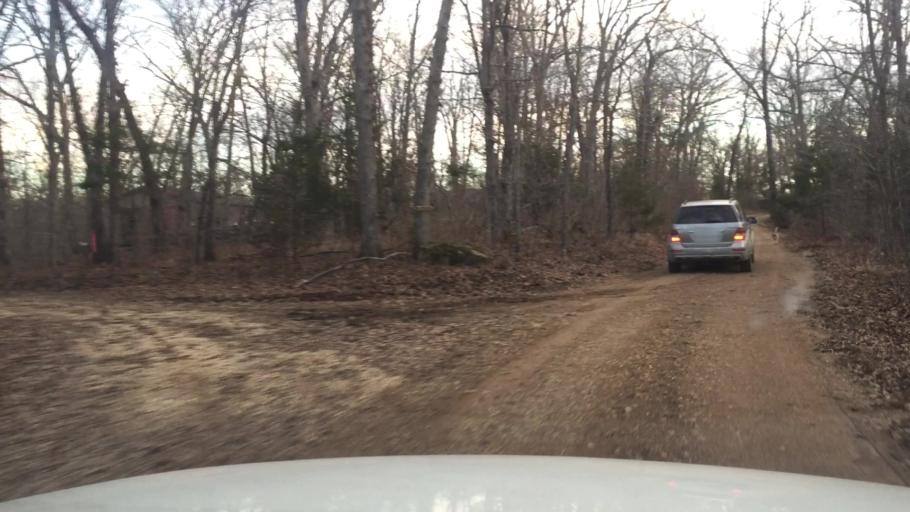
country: US
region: Missouri
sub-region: Camden County
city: Four Seasons
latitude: 38.3102
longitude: -92.7507
